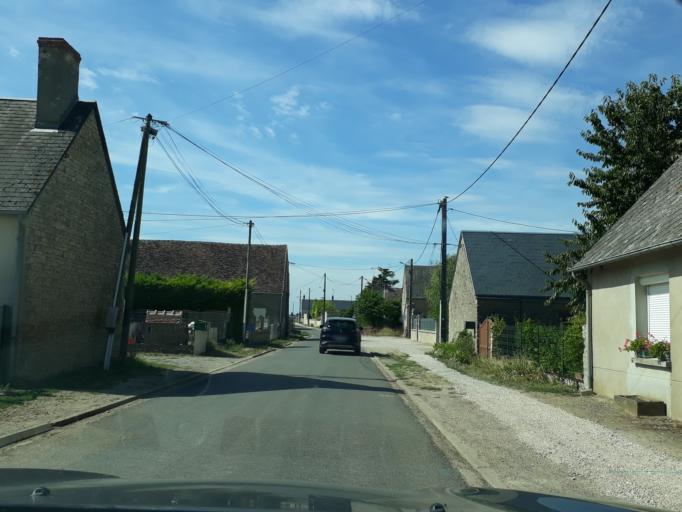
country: FR
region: Centre
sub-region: Departement du Loir-et-Cher
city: Ouzouer-le-Marche
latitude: 47.9401
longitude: 1.5377
